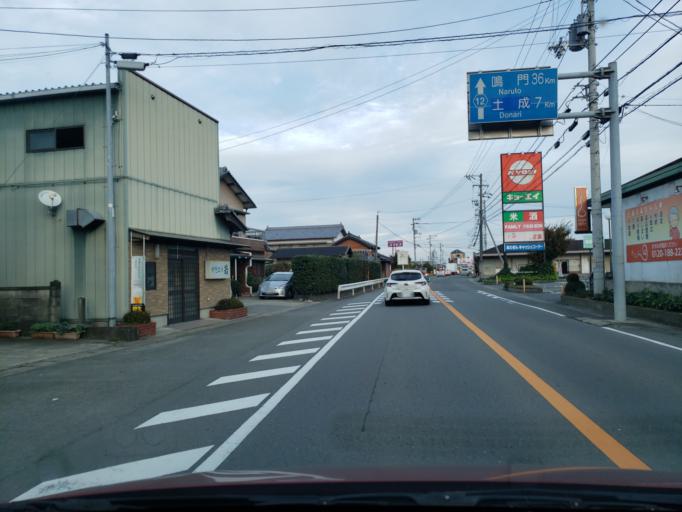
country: JP
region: Tokushima
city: Kamojimacho-jogejima
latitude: 34.0840
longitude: 134.2766
